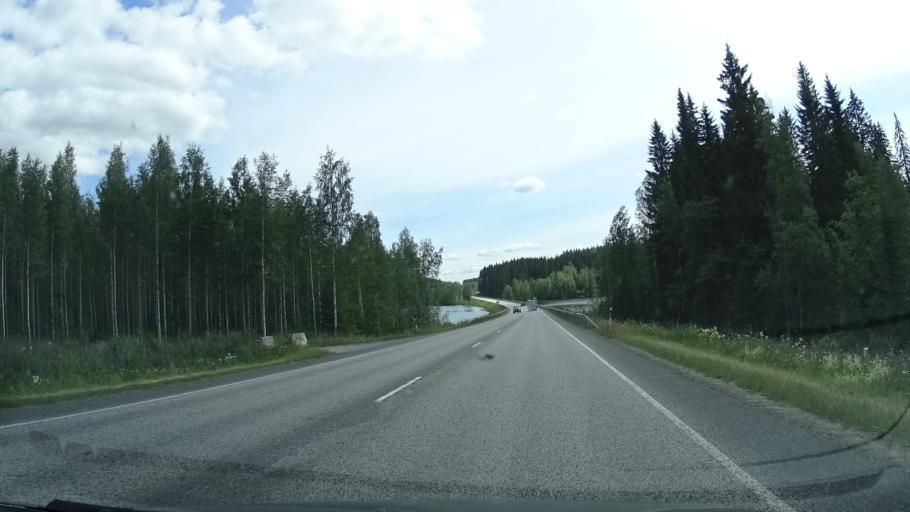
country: FI
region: Central Finland
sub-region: Jyvaeskylae
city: Jyvaeskylae
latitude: 62.2585
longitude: 25.6093
